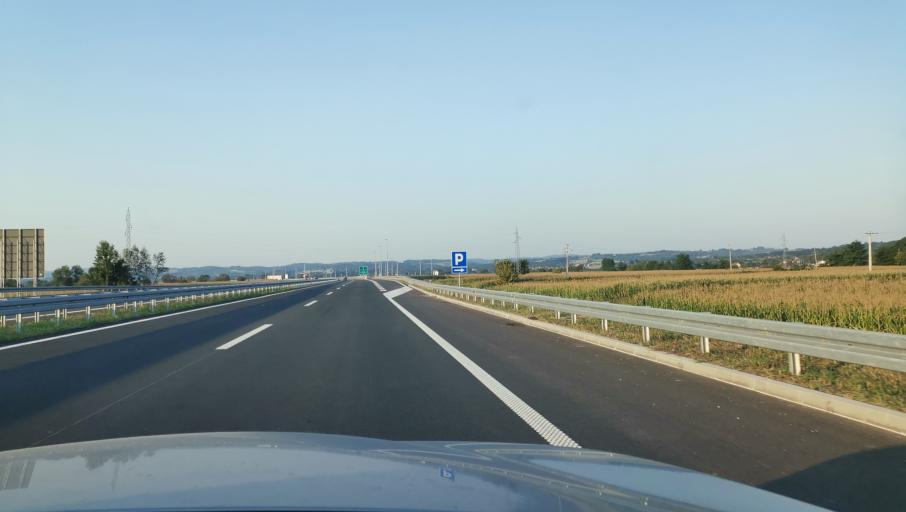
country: RS
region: Central Serbia
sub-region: Kolubarski Okrug
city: Ljig
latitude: 44.2385
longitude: 20.2590
